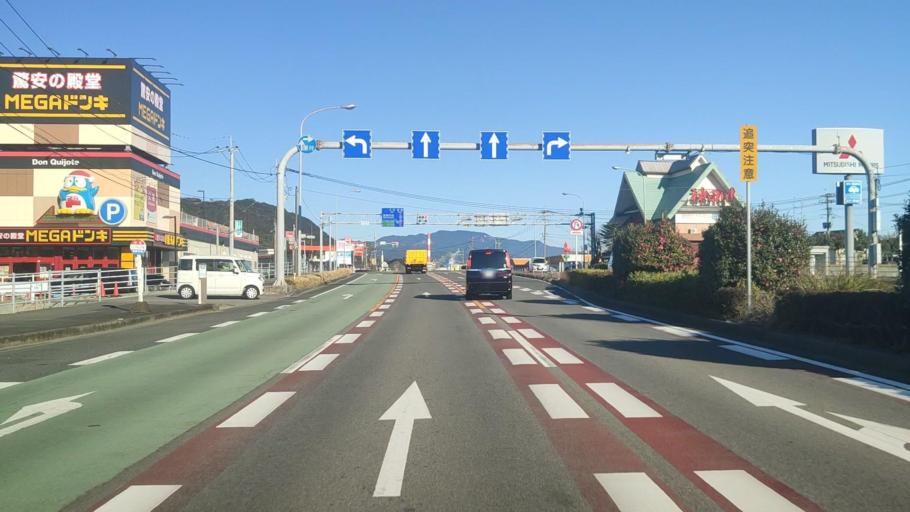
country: JP
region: Miyazaki
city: Nobeoka
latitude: 32.5439
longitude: 131.6781
